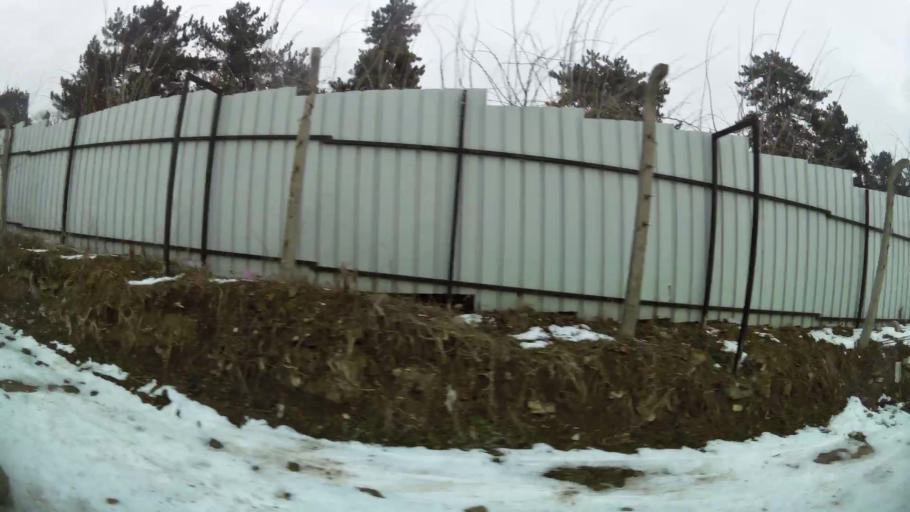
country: MK
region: Suto Orizari
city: Suto Orizare
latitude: 42.0374
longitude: 21.4321
